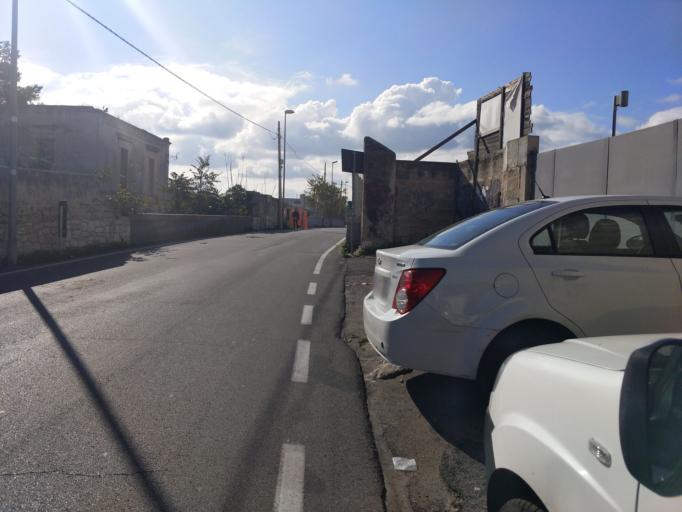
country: IT
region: Apulia
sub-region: Provincia di Bari
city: Bari
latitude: 41.1150
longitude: 16.8574
